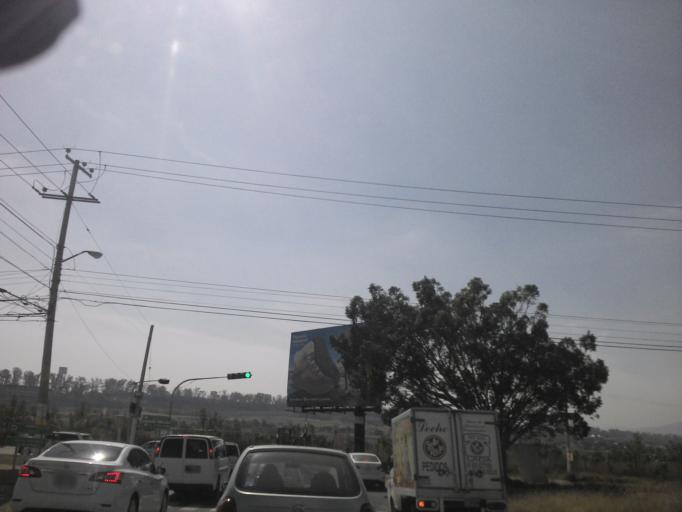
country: MX
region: Jalisco
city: Zapopan2
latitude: 20.7216
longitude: -103.4305
